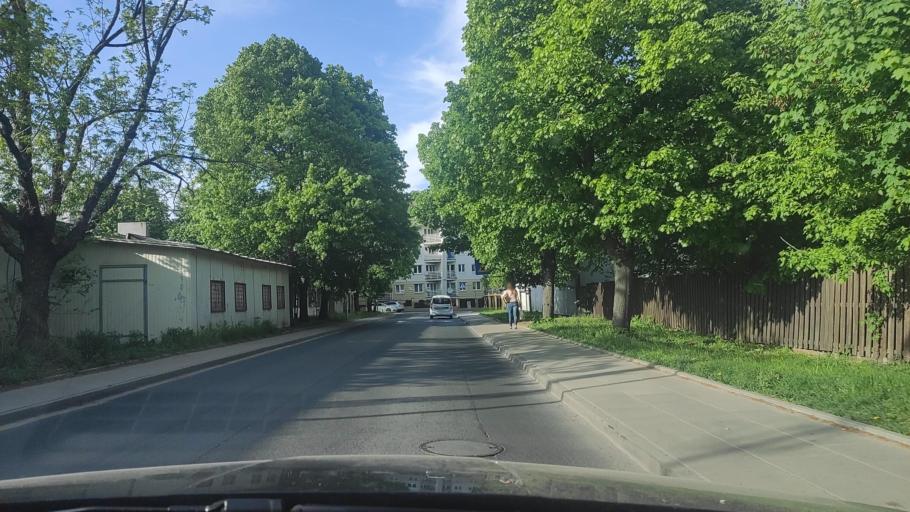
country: PL
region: Greater Poland Voivodeship
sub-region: Powiat poznanski
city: Czerwonak
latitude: 52.4439
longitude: 16.9496
